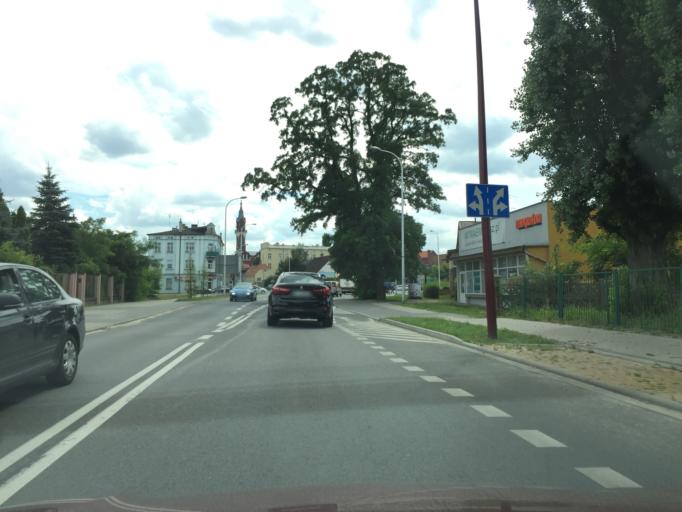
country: PL
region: Greater Poland Voivodeship
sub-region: Kalisz
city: Kalisz
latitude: 51.7526
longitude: 18.0946
